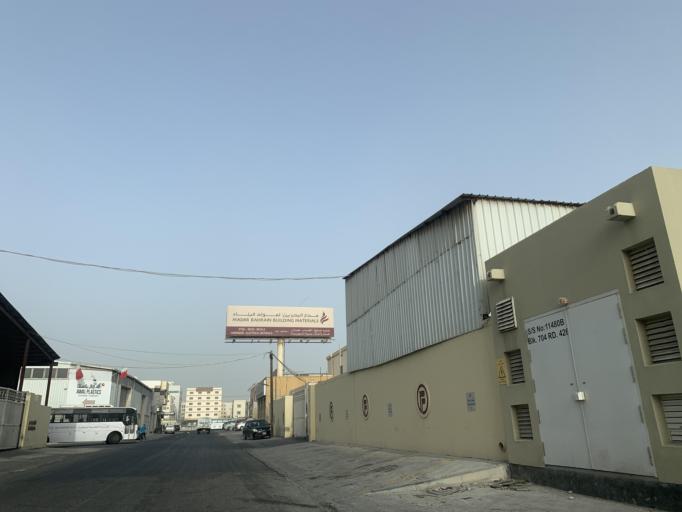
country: BH
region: Northern
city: Madinat `Isa
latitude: 26.1808
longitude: 50.5332
